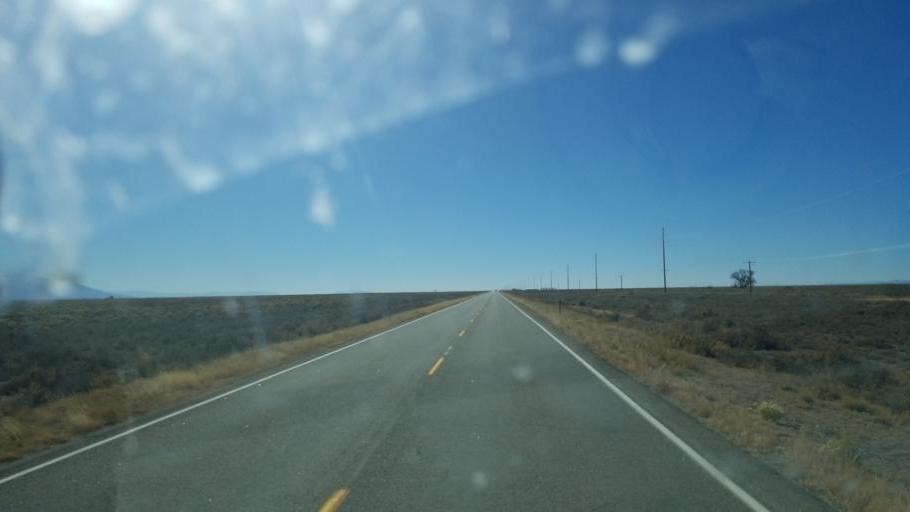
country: US
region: Colorado
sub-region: Saguache County
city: Saguache
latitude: 37.9683
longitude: -105.9051
